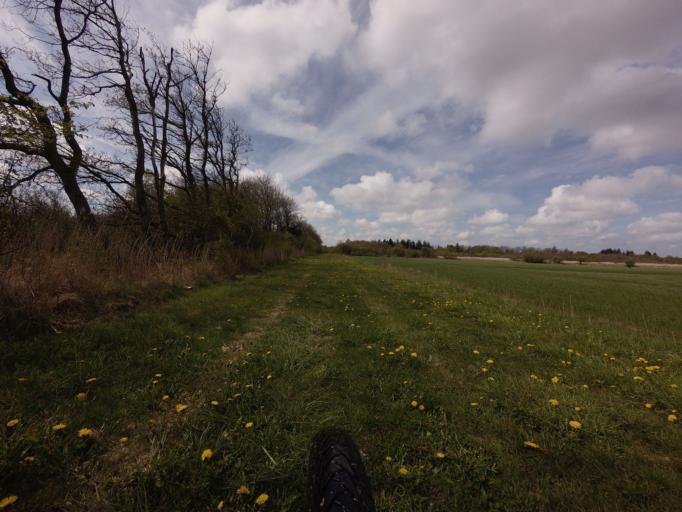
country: DK
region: North Denmark
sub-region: Jammerbugt Kommune
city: Kas
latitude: 57.1945
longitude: 9.6113
